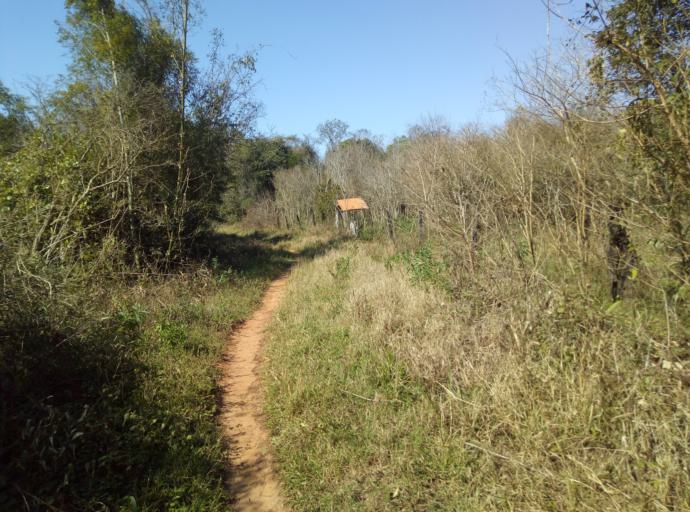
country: PY
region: Caaguazu
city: Doctor Cecilio Baez
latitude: -25.1793
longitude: -56.2231
